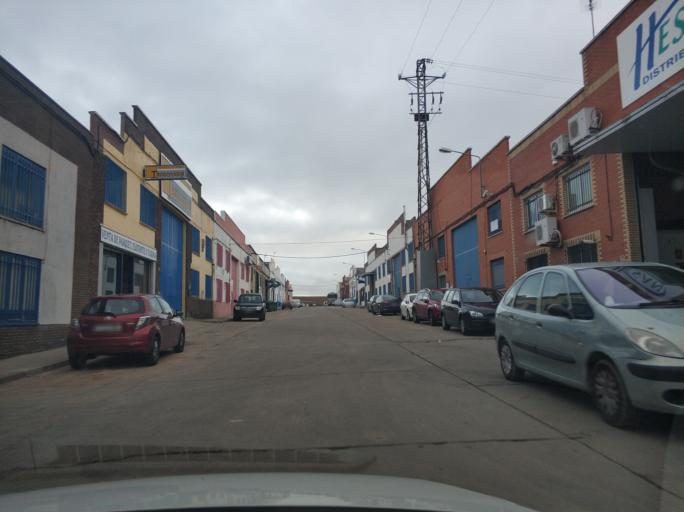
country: ES
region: Castille and Leon
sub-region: Provincia de Salamanca
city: Villares de la Reina
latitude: 40.9917
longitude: -5.6383
